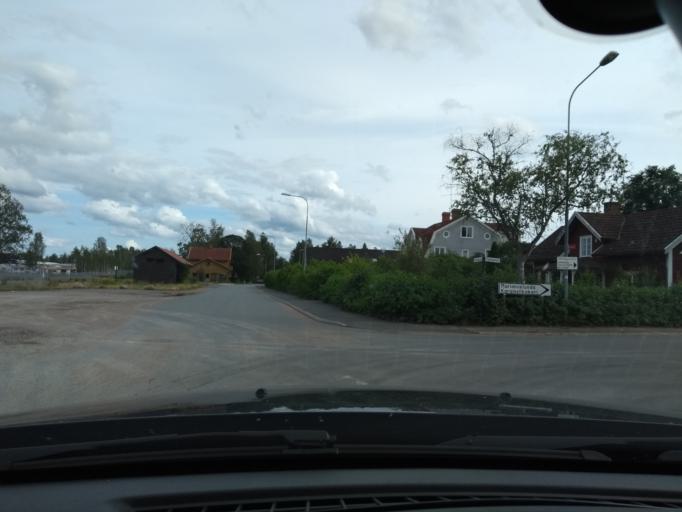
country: SE
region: Joenkoeping
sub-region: Eksjo Kommun
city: Mariannelund
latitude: 57.6171
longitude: 15.5827
